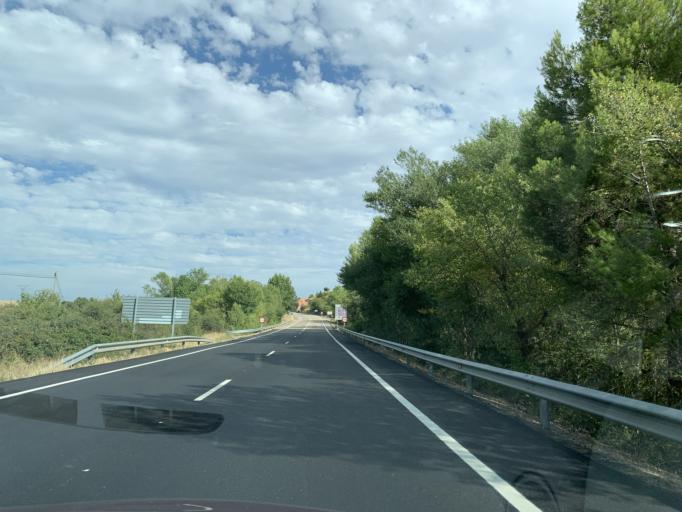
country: ES
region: Aragon
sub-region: Provincia de Huesca
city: Ayerbe
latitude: 42.2804
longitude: -0.6955
